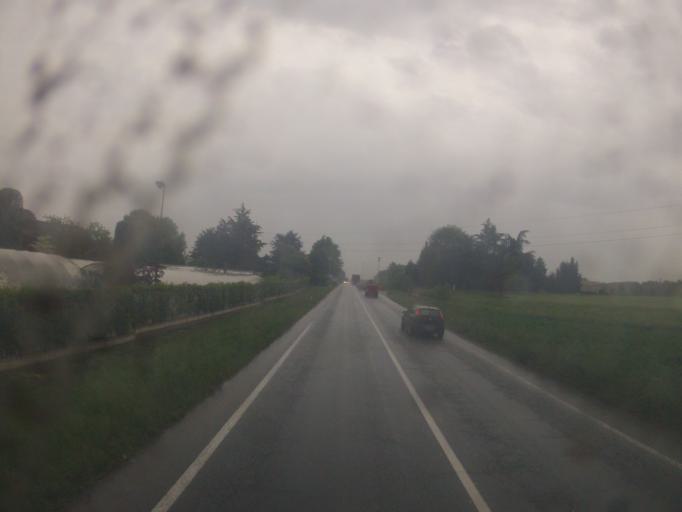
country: IT
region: Piedmont
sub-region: Provincia di Torino
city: La Loggia
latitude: 44.9345
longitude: 7.6715
